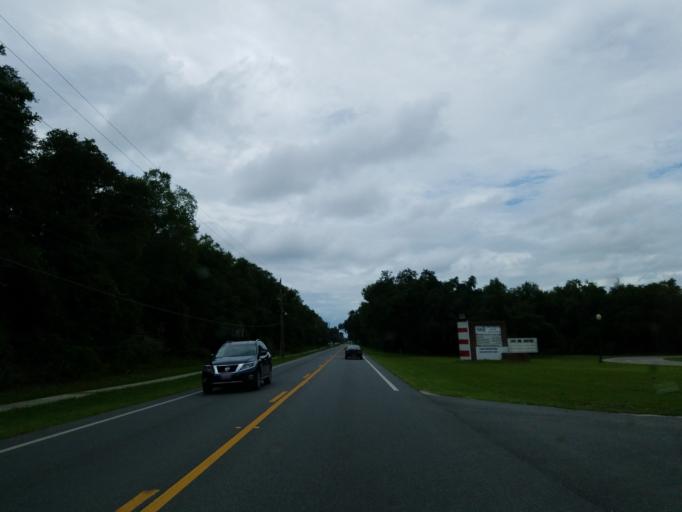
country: US
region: Florida
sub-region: Sumter County
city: Lake Panasoffkee
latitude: 28.7643
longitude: -82.1161
